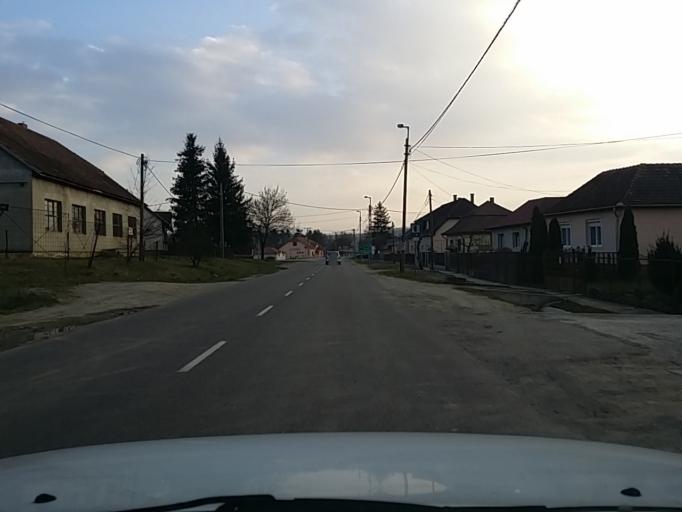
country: HU
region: Heves
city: Petervasara
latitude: 48.0196
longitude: 20.1076
